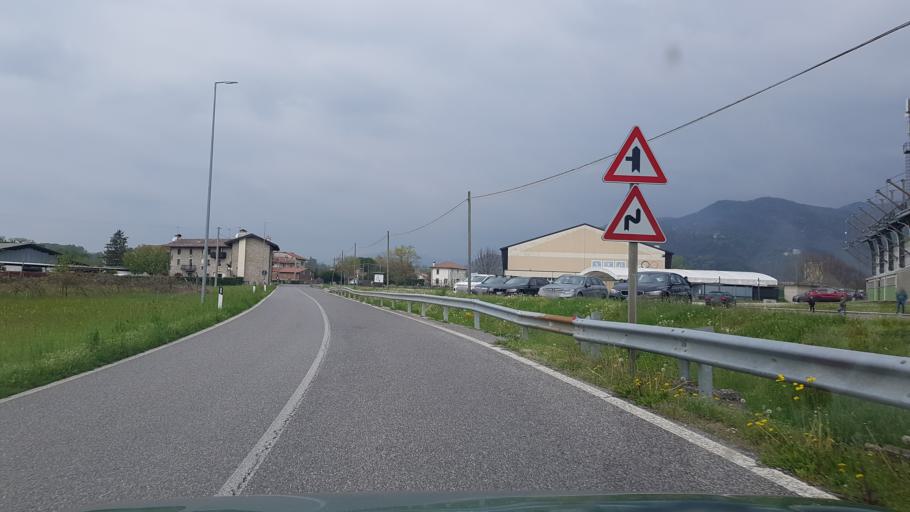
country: IT
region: Friuli Venezia Giulia
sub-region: Provincia di Udine
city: Faedis
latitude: 46.1390
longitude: 13.3505
